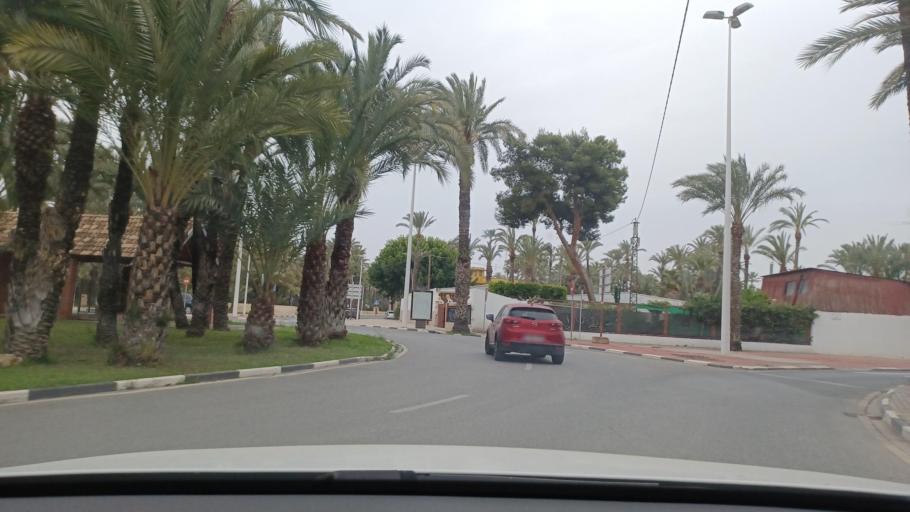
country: ES
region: Valencia
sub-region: Provincia de Alicante
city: Elche
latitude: 38.2572
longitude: -0.6925
